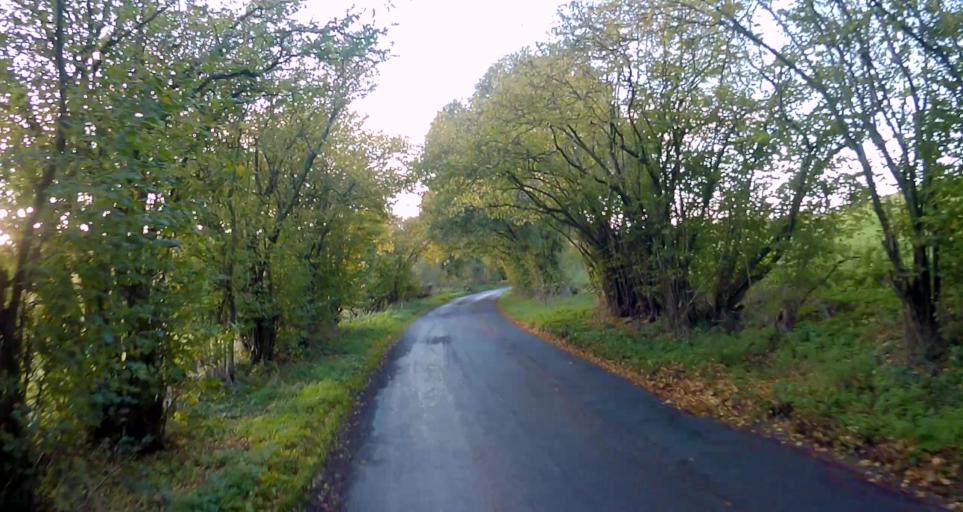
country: GB
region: England
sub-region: Hampshire
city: Basingstoke
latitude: 51.1905
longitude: -1.0774
